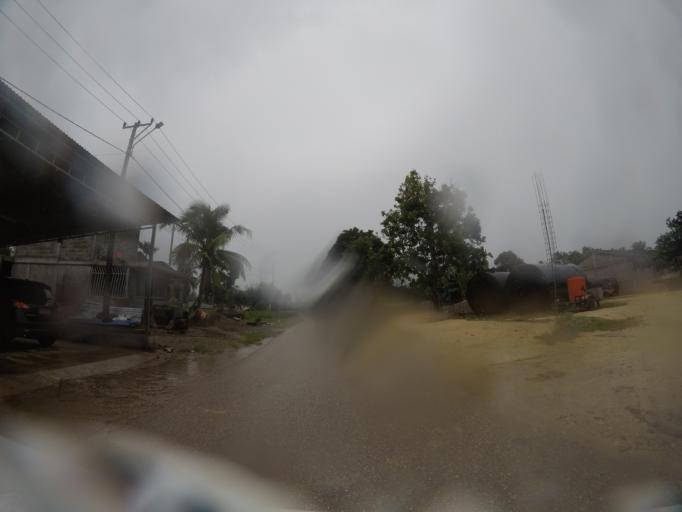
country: TL
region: Lautem
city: Lospalos
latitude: -8.5203
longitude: 127.0022
